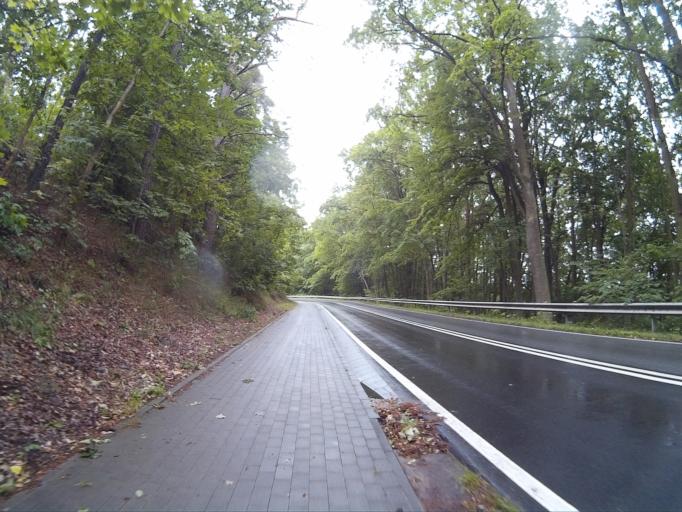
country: PL
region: Kujawsko-Pomorskie
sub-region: Powiat swiecki
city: Osie
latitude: 53.6156
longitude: 18.2763
